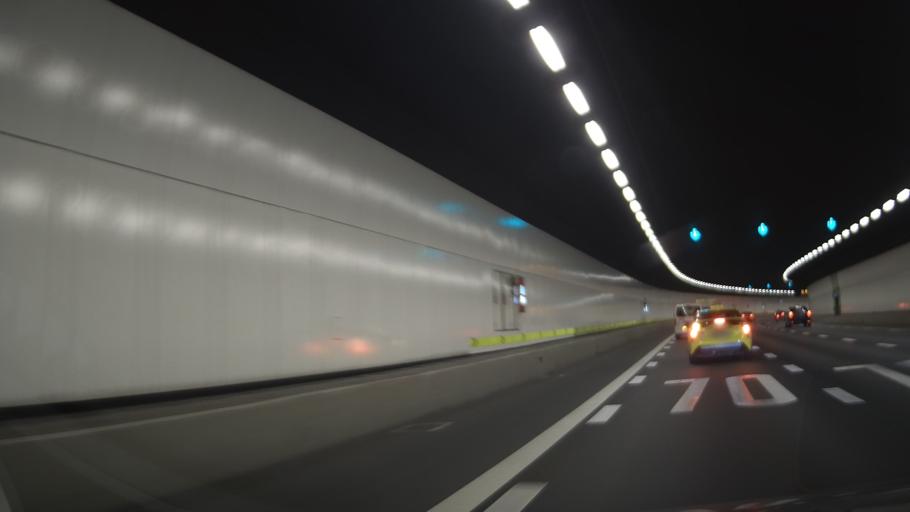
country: SG
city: Singapore
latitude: 1.3138
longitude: 103.8907
